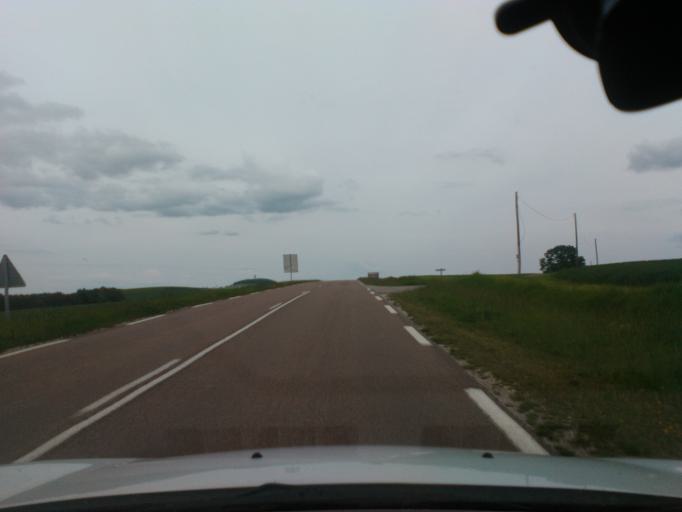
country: FR
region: Champagne-Ardenne
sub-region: Departement de l'Aube
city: Ville-sous-la-Ferte
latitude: 48.2170
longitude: 4.8247
